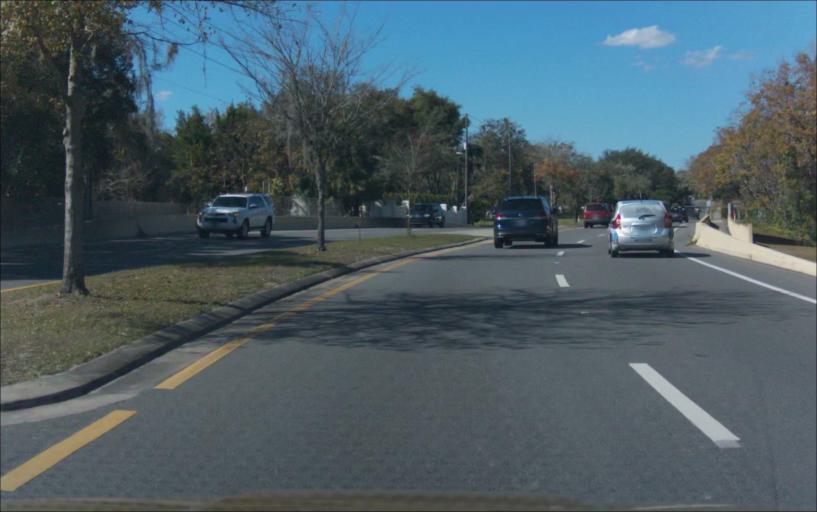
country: US
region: Florida
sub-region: Orange County
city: Winter Park
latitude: 28.6255
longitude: -81.3275
